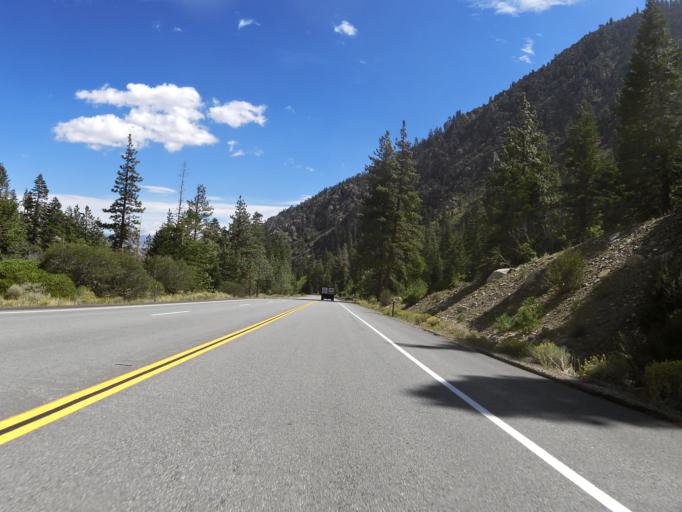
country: US
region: Nevada
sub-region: Douglas County
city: Gardnerville Ranchos
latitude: 38.7641
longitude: -119.8594
